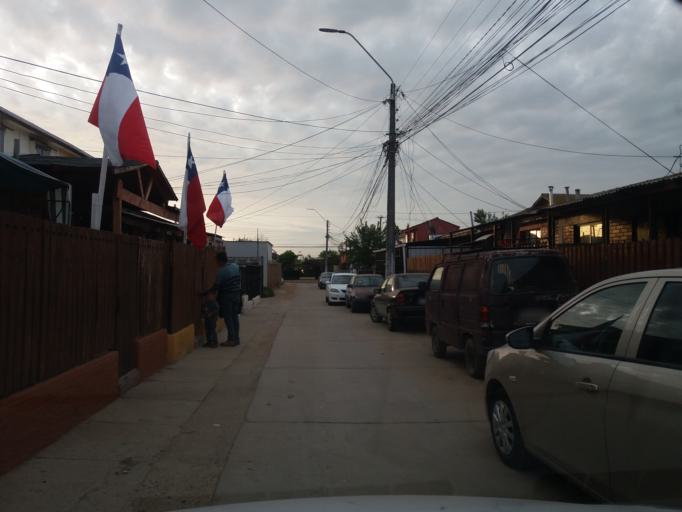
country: CL
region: Valparaiso
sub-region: Provincia de Marga Marga
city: Limache
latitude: -33.0094
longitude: -71.2566
